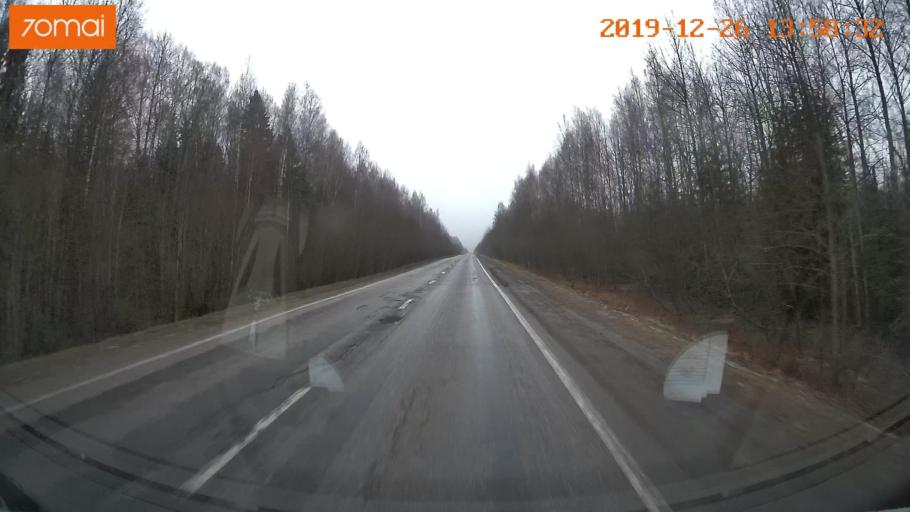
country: RU
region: Jaroslavl
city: Poshekhon'ye
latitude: 58.5733
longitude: 38.7030
